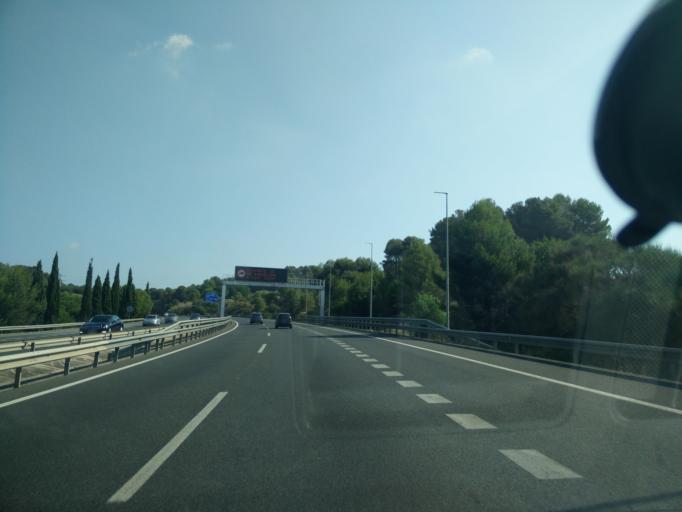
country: ES
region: Catalonia
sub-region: Provincia de Barcelona
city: Rubi
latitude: 41.5006
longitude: 2.0503
